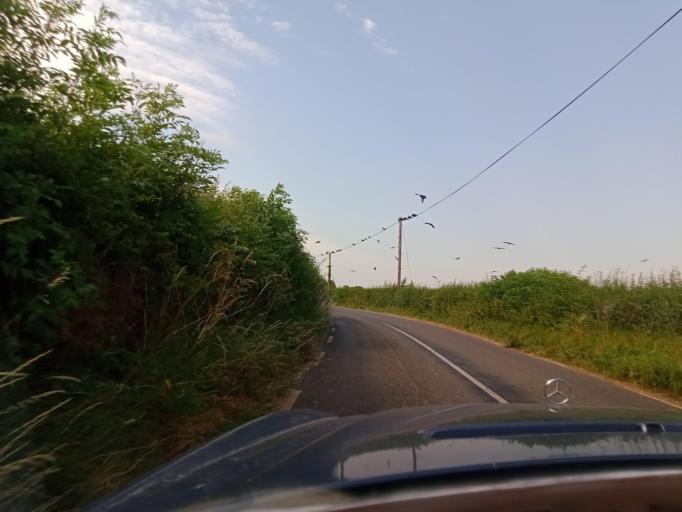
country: IE
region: Leinster
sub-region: Kilkenny
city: Callan
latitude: 52.5090
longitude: -7.3121
